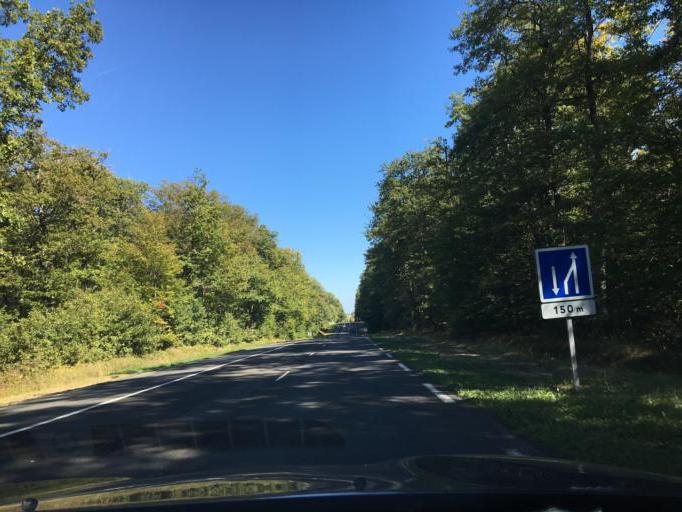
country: FR
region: Centre
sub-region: Departement d'Indre-et-Loire
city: Cheille
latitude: 47.2393
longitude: 0.4222
